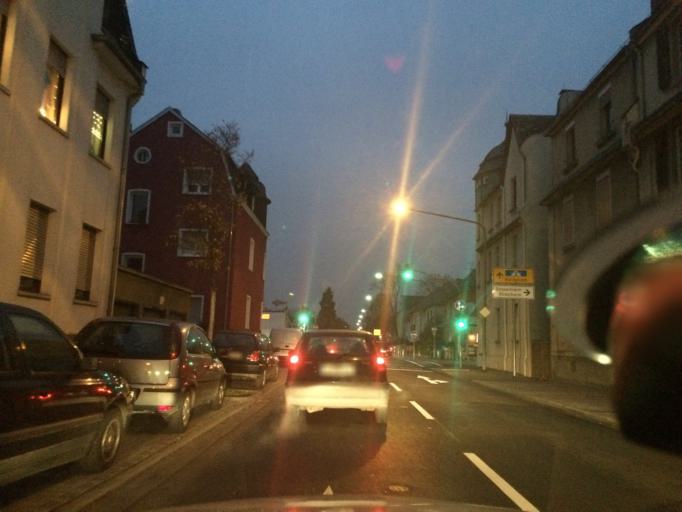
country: DE
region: Hesse
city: Sulzbach
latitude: 50.1116
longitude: 8.5395
